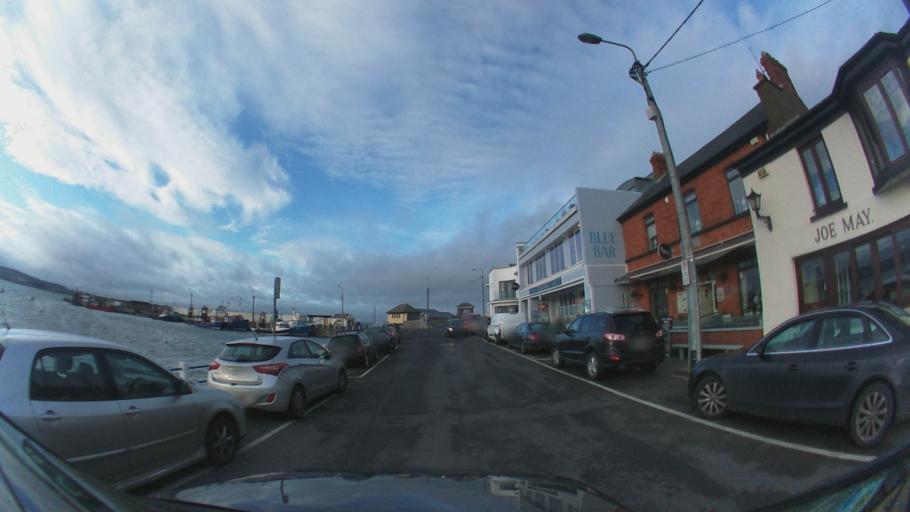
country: IE
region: Leinster
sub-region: Fingal County
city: Skerries
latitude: 53.5846
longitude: -6.1050
